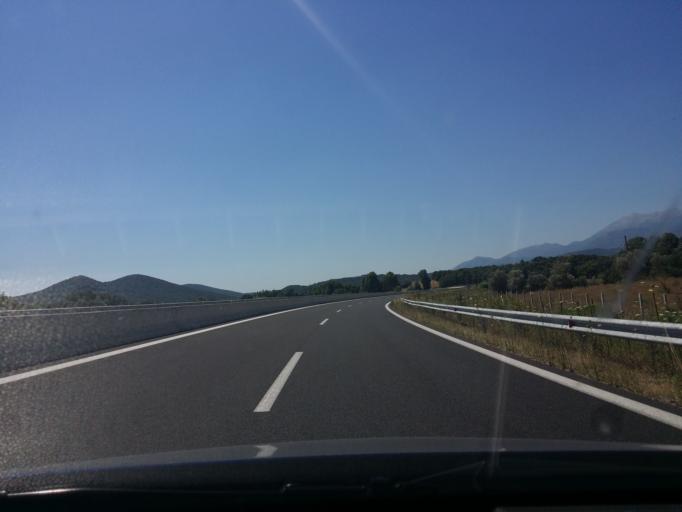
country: GR
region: Peloponnese
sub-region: Nomos Lakonias
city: Magoula
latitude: 37.1860
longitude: 22.3579
